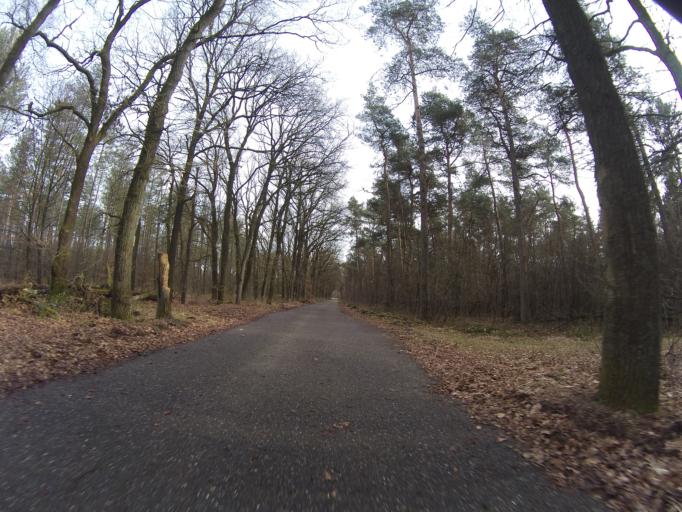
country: NL
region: Utrecht
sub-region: Gemeente Utrechtse Heuvelrug
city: Maarn
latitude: 52.1011
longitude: 5.3236
